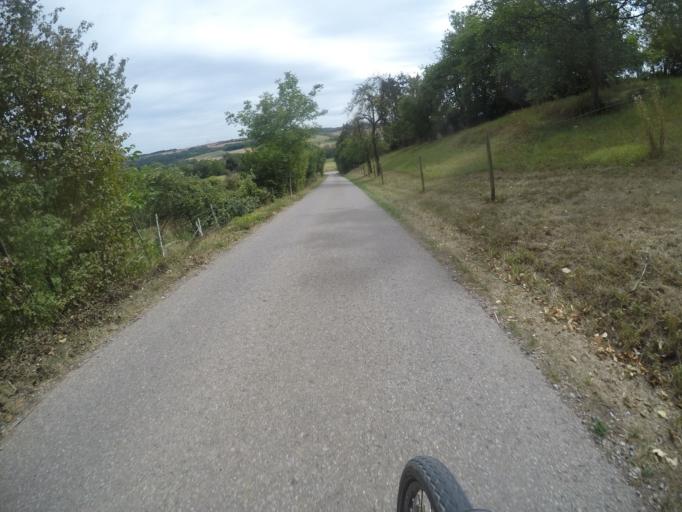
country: DE
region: Baden-Wuerttemberg
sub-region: Regierungsbezirk Stuttgart
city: Oberriexingen
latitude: 48.9290
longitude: 8.9970
